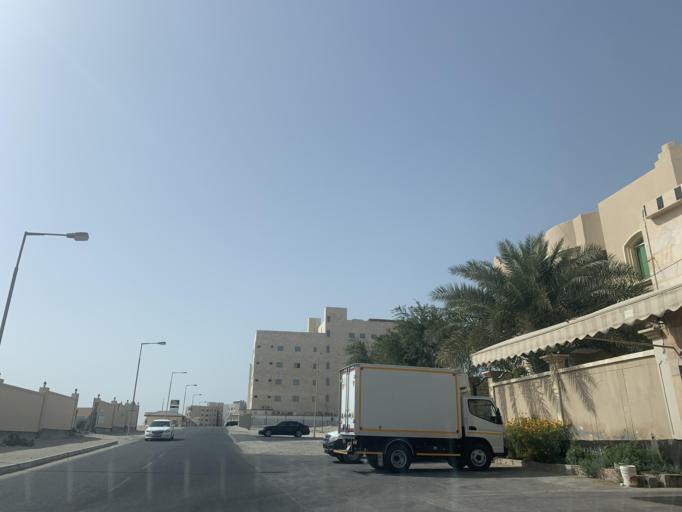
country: BH
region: Northern
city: Ar Rifa'
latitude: 26.1496
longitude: 50.5690
